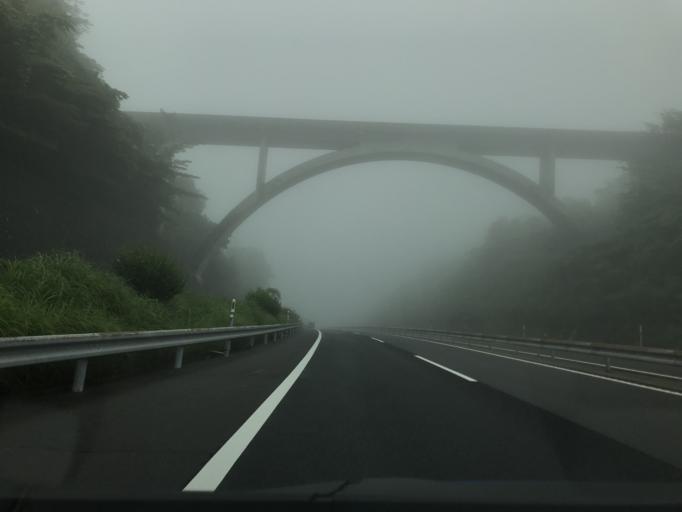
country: JP
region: Oita
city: Hiji
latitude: 33.3630
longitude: 131.4516
